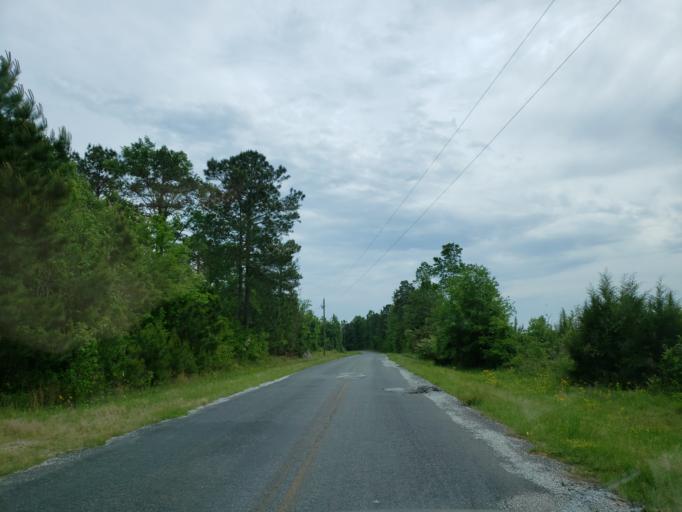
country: US
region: Georgia
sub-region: Bibb County
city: West Point
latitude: 32.8568
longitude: -83.8919
